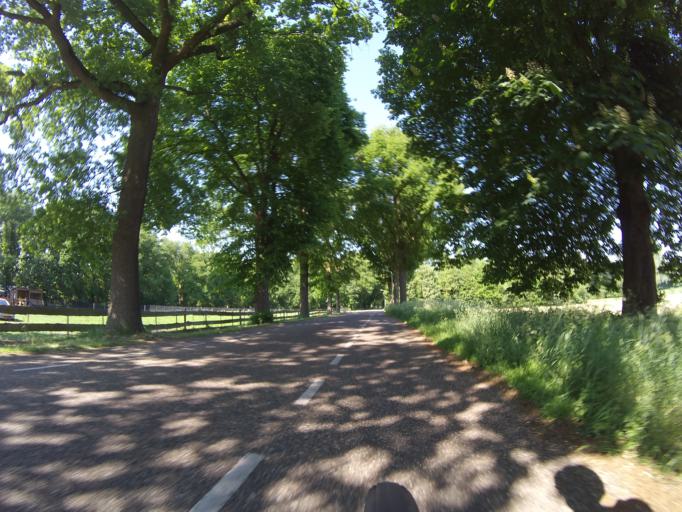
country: NL
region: Drenthe
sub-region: Gemeente Coevorden
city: Sleen
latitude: 52.7313
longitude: 6.7988
